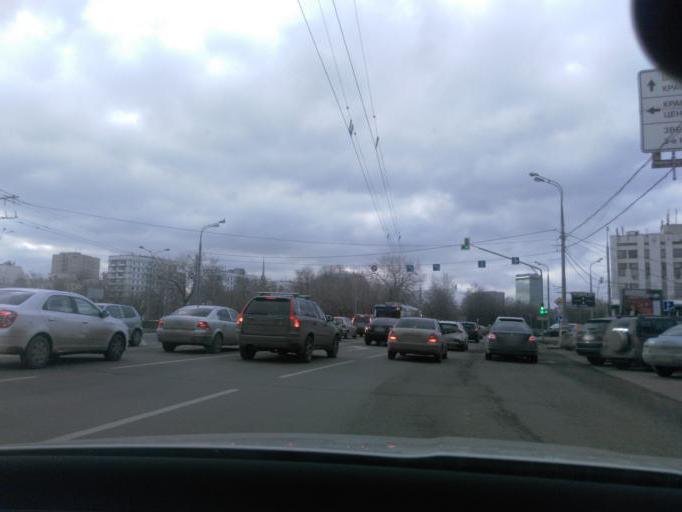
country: RU
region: Moskovskaya
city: Dorogomilovo
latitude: 55.7642
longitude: 37.5609
